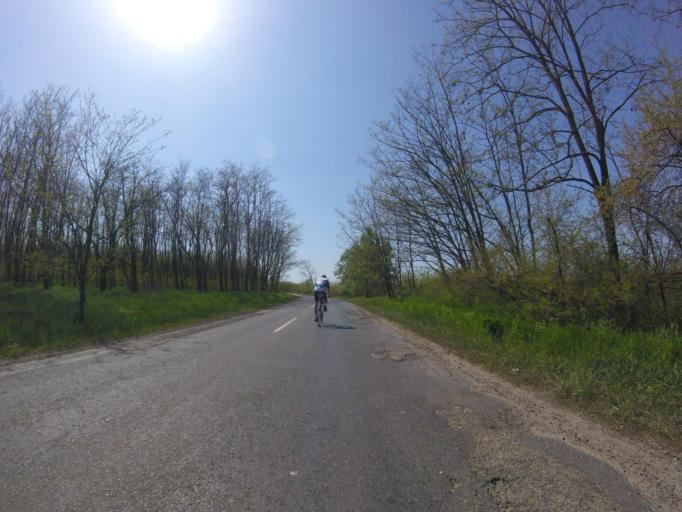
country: HU
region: Pest
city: Ujhartyan
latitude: 47.2279
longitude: 19.4179
